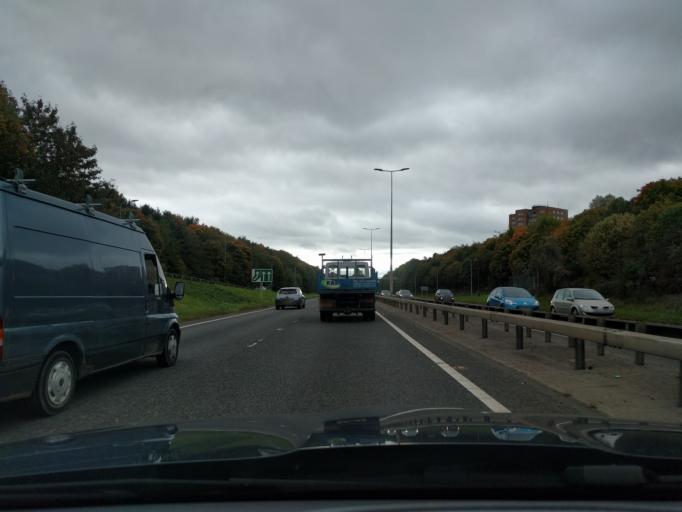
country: GB
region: England
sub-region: Newcastle upon Tyne
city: Benwell
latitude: 54.9945
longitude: -1.6817
